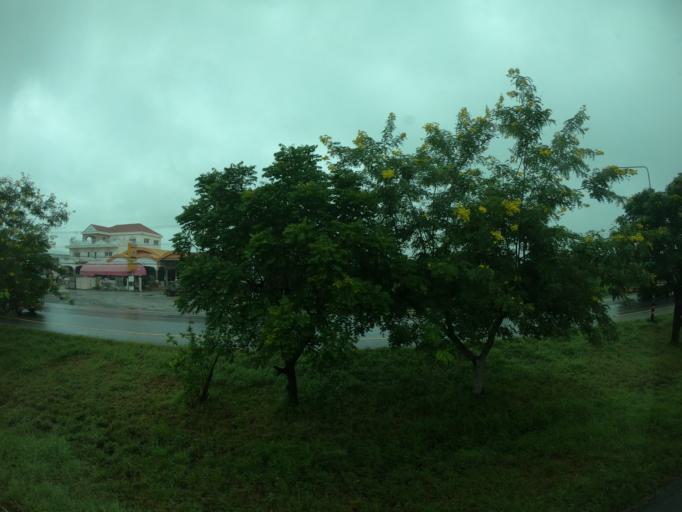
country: TH
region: Nakhon Ratchasima
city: Phimai
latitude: 15.2529
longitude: 102.4103
